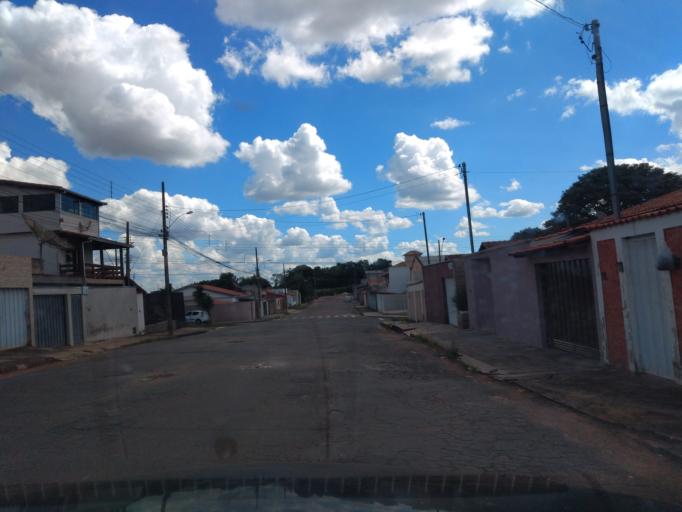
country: BR
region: Minas Gerais
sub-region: Tres Coracoes
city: Tres Coracoes
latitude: -21.6833
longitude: -45.2693
